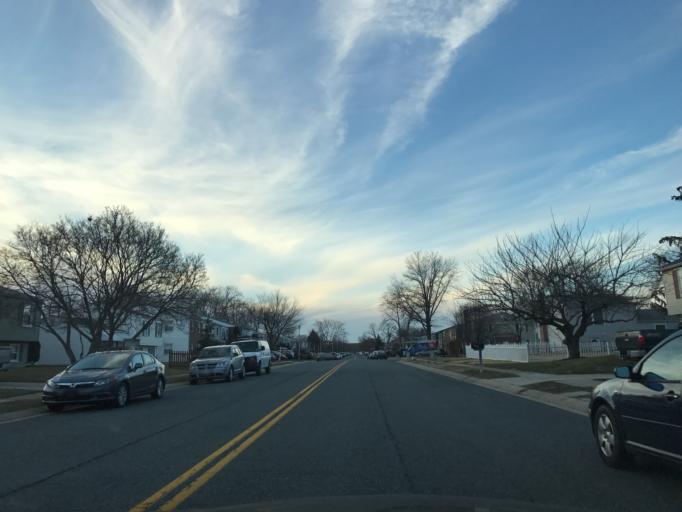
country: US
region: Maryland
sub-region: Harford County
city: Joppatowne
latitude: 39.4065
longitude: -76.3565
